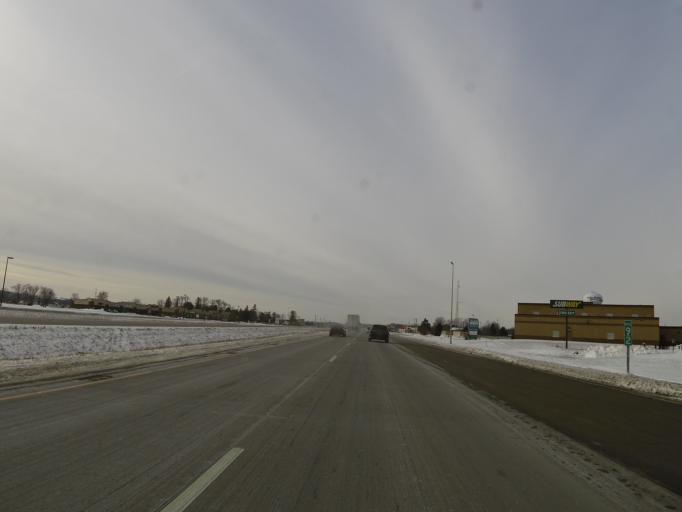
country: US
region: Minnesota
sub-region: Scott County
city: Belle Plaine
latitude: 44.6205
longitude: -93.7545
